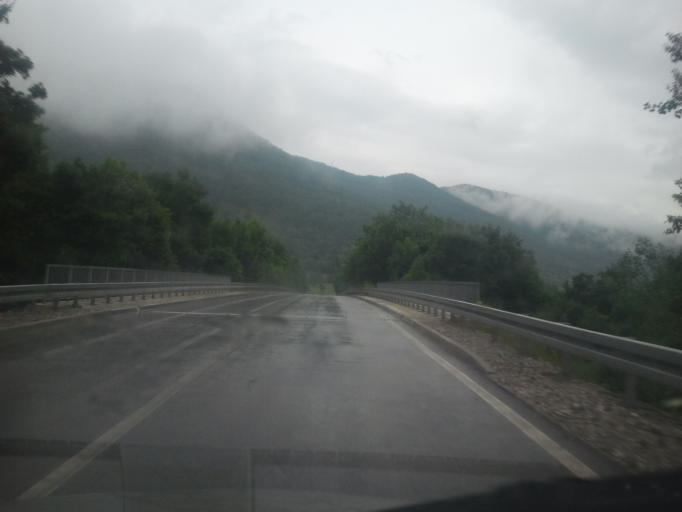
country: HR
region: Zadarska
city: Gracac
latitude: 44.3180
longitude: 15.7770
